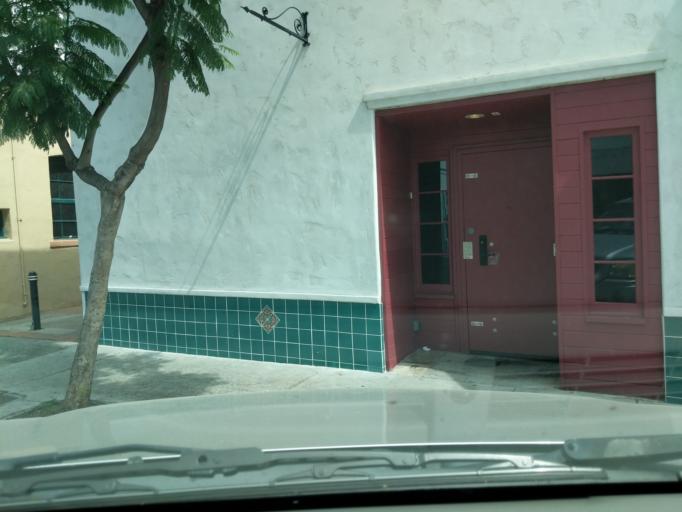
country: US
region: California
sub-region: Santa Barbara County
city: Santa Barbara
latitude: 34.4190
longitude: -119.6977
